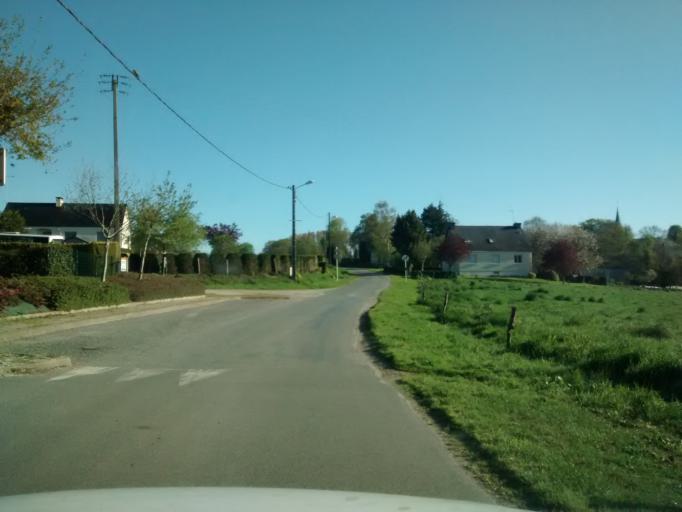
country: FR
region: Brittany
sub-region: Departement du Morbihan
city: Malestroit
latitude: 47.8537
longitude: -2.4121
